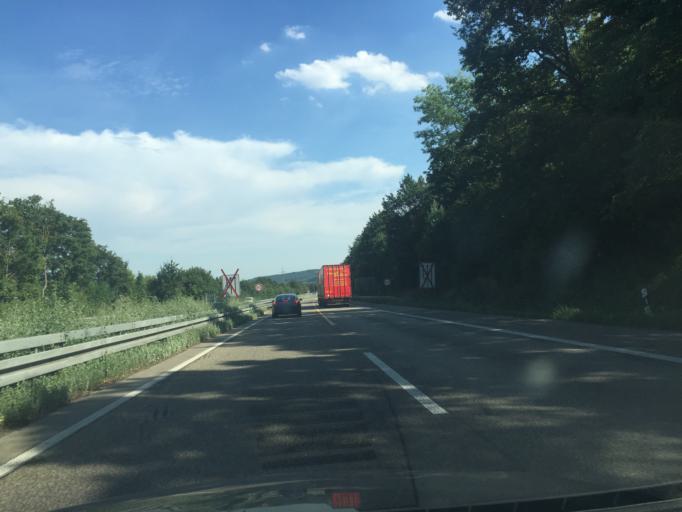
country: DE
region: Hesse
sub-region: Regierungsbezirk Giessen
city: Wetzlar
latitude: 50.5879
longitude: 8.5286
